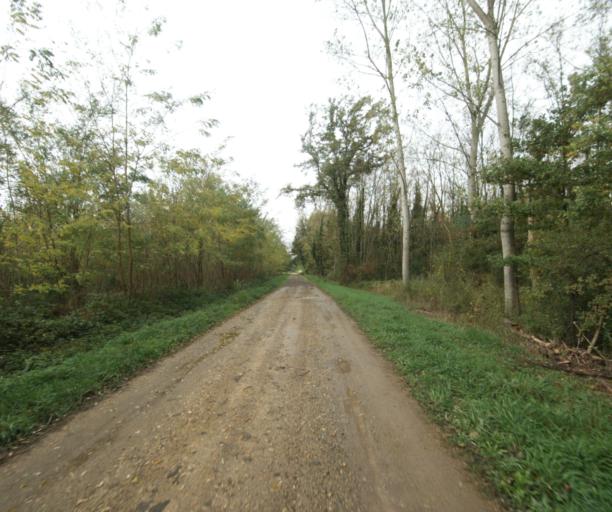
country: FR
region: Rhone-Alpes
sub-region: Departement de l'Ain
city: Pont-de-Vaux
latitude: 46.4633
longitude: 4.9043
